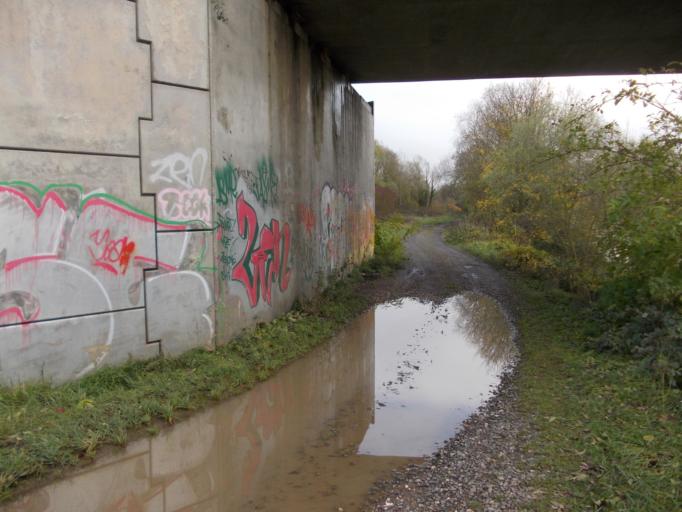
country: FR
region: Lorraine
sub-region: Departement de Meurthe-et-Moselle
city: Bouxieres-aux-Dames
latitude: 48.7467
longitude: 6.1661
